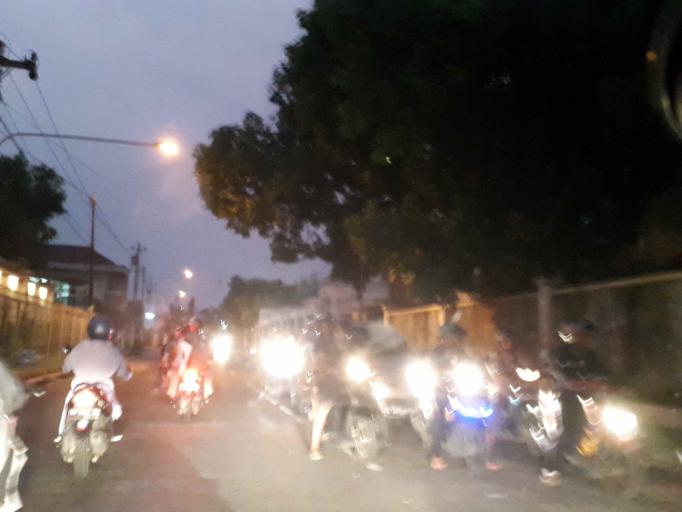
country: ID
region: Central Java
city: Surakarta
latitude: -7.5585
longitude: 110.8285
